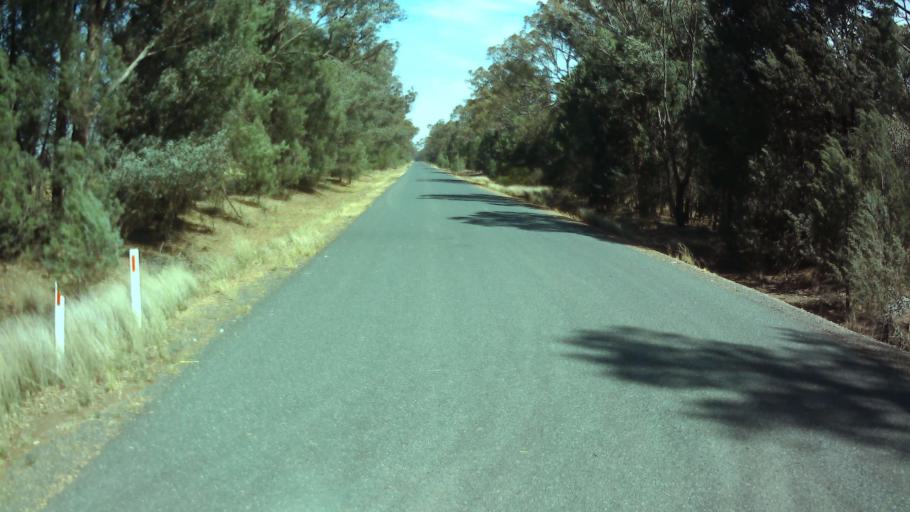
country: AU
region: New South Wales
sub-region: Weddin
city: Grenfell
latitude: -34.0584
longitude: 148.1314
